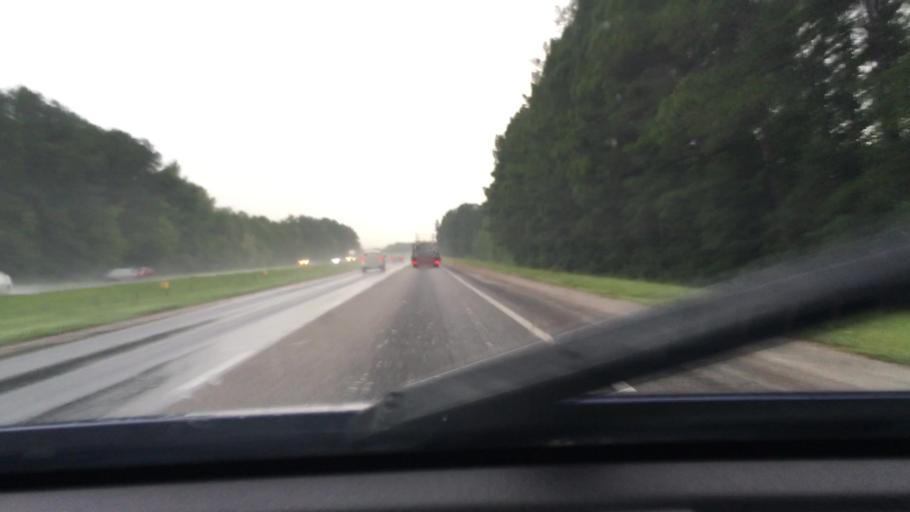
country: US
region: South Carolina
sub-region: Lee County
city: Bishopville
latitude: 34.1949
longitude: -80.1318
